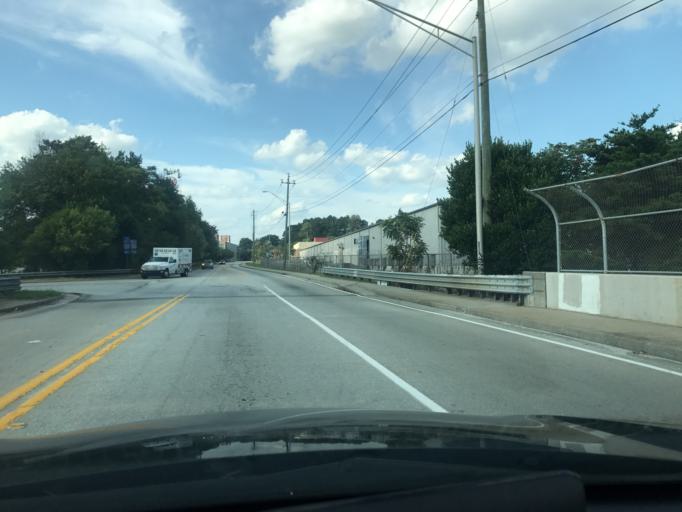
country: US
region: Georgia
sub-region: Fulton County
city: Atlanta
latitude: 33.7437
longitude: -84.3582
